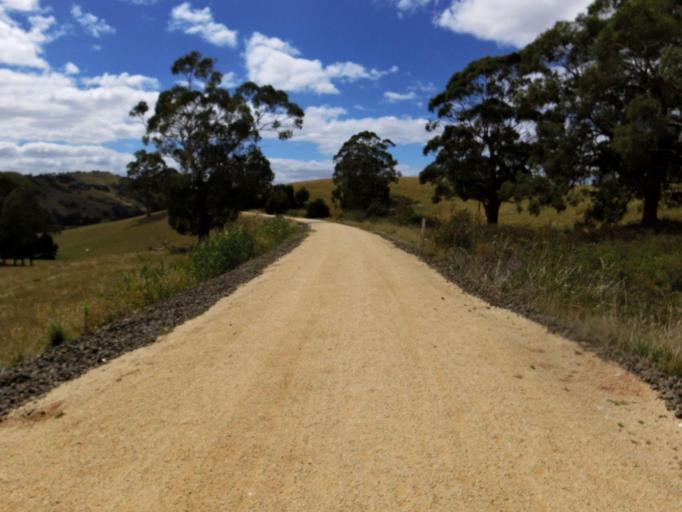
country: AU
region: Victoria
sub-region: Baw Baw
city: Warragul
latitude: -38.4291
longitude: 145.8554
